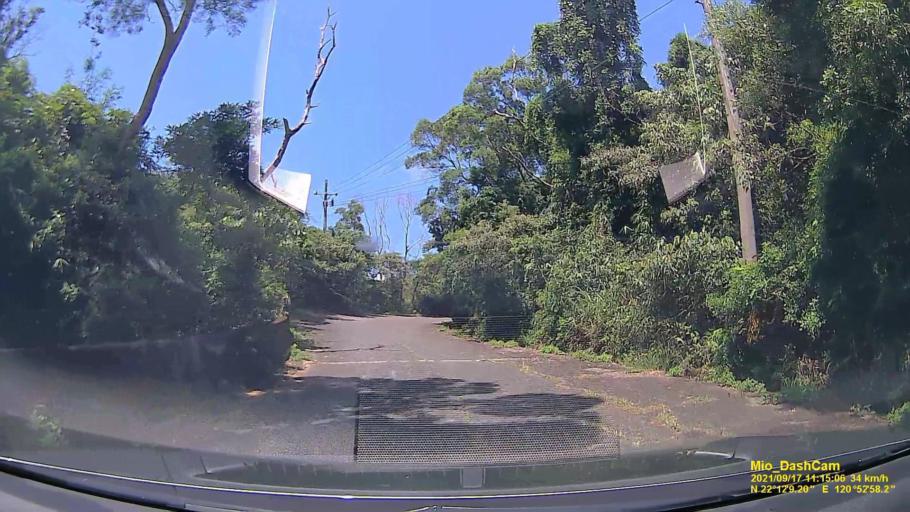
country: TW
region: Taiwan
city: Hengchun
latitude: 22.2026
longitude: 120.8828
